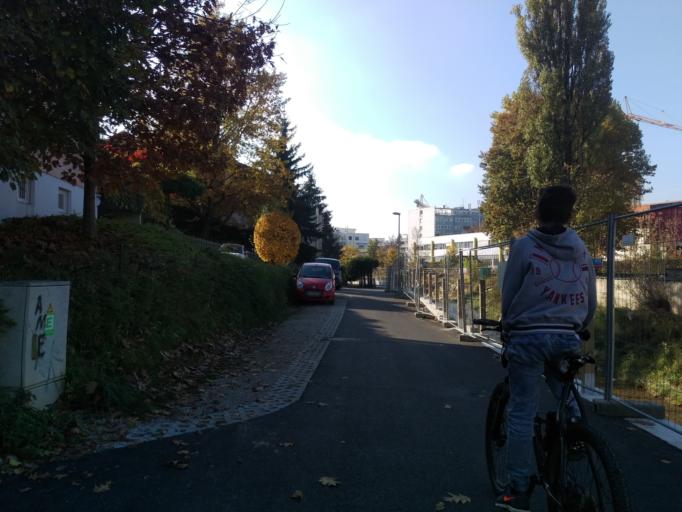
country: AT
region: Styria
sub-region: Graz Stadt
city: Graz
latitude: 47.0762
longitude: 15.4663
